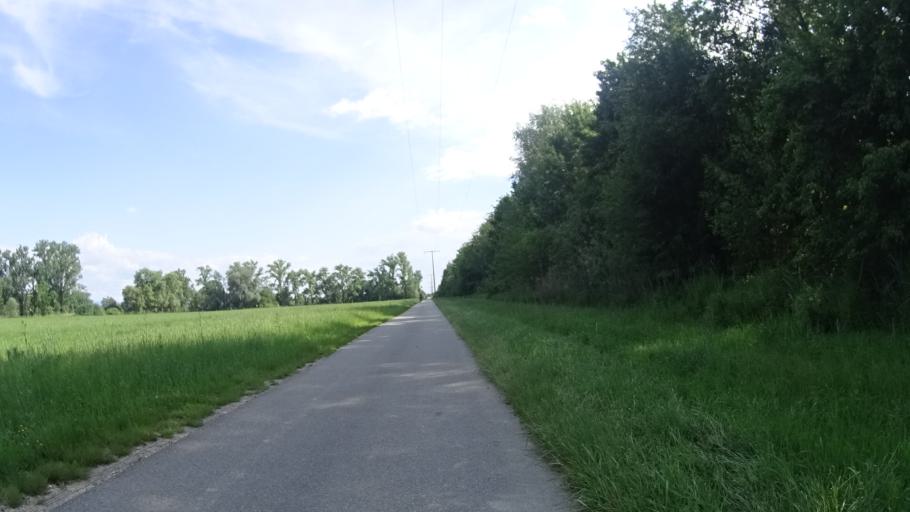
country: DE
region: Baden-Wuerttemberg
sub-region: Freiburg Region
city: Breisach am Rhein
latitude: 48.0720
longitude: 7.5910
